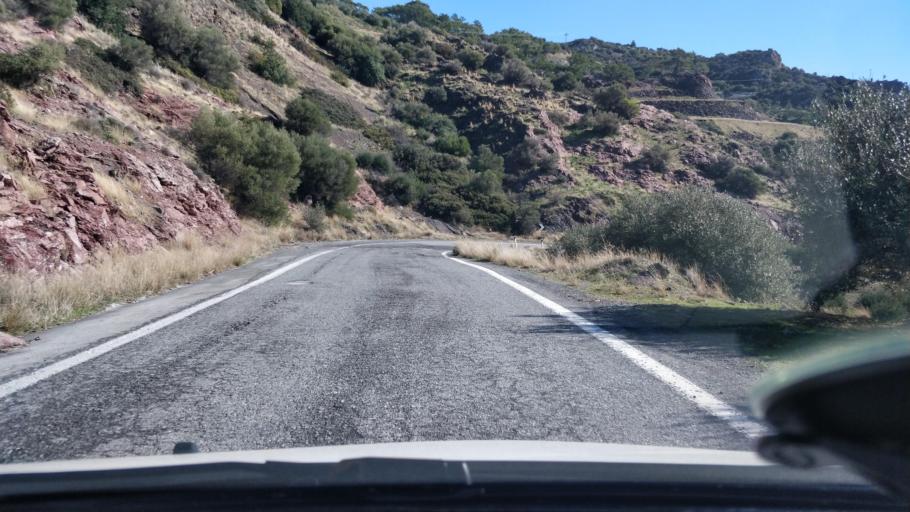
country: GR
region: Crete
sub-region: Nomos Irakleiou
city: Arkalochori
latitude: 35.0061
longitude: 25.4341
